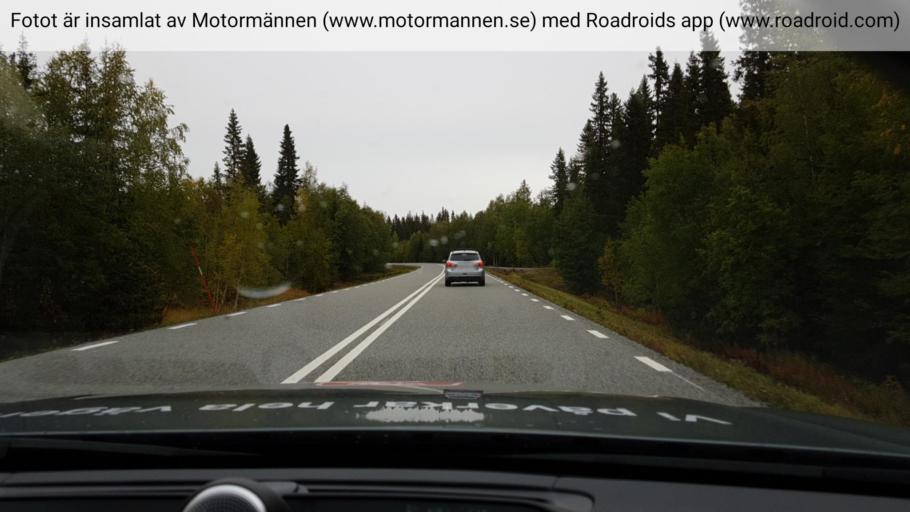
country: SE
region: Jaemtland
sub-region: Stroemsunds Kommun
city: Stroemsund
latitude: 64.0694
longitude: 15.5579
